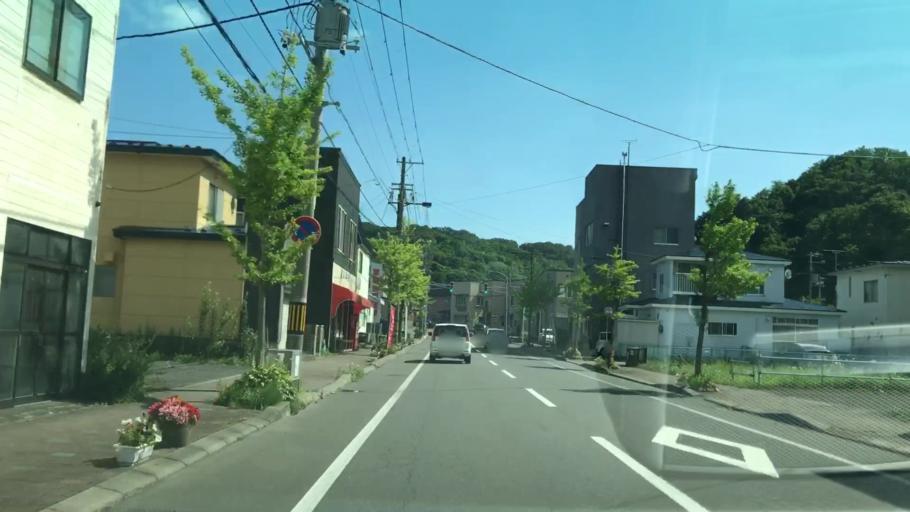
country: JP
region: Hokkaido
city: Muroran
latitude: 42.3137
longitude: 140.9911
